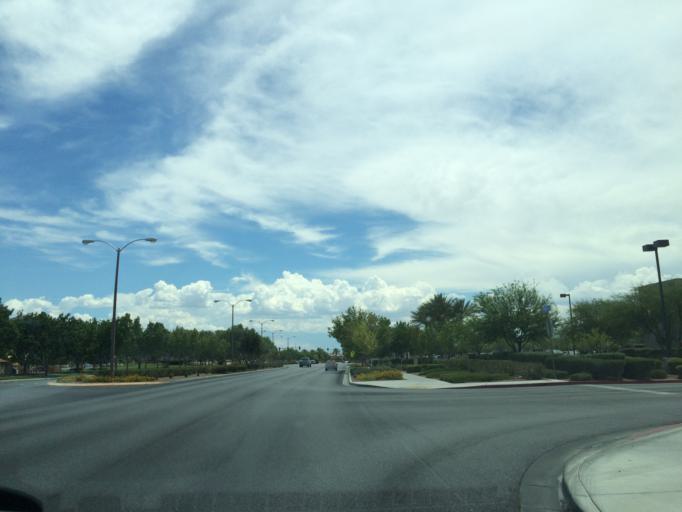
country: US
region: Nevada
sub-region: Clark County
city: North Las Vegas
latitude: 36.2863
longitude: -115.1774
